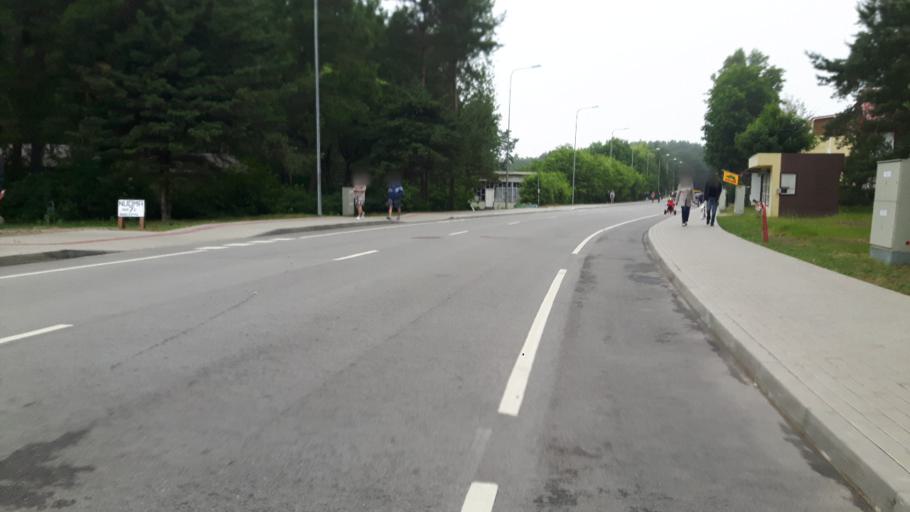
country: LT
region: Klaipedos apskritis
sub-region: Palanga
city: Sventoji
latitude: 56.0248
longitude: 21.0792
